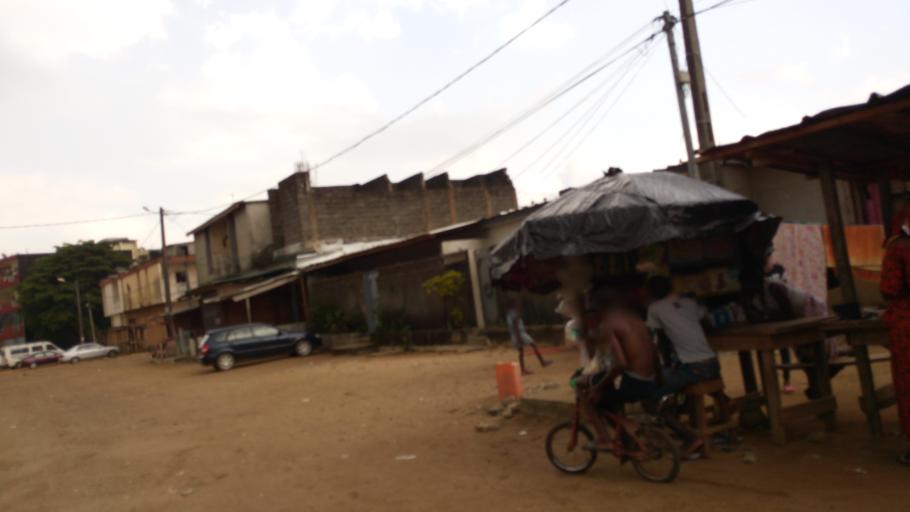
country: CI
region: Lagunes
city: Abobo
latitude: 5.4014
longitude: -4.0036
